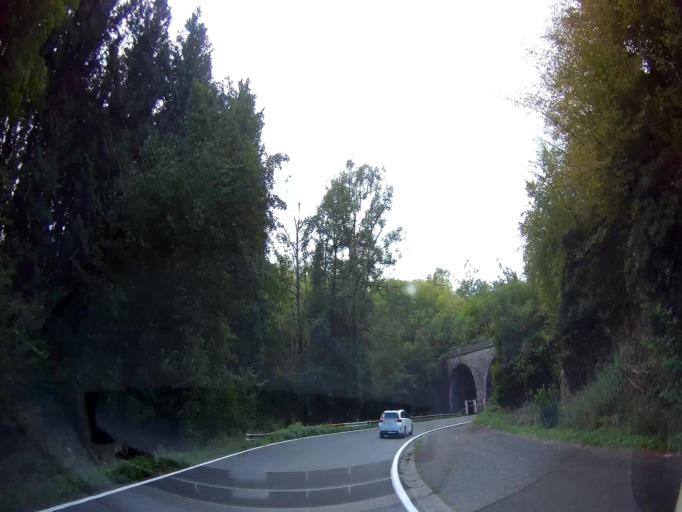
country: BE
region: Wallonia
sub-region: Province de Namur
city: Onhaye
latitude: 50.2956
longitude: 4.8151
